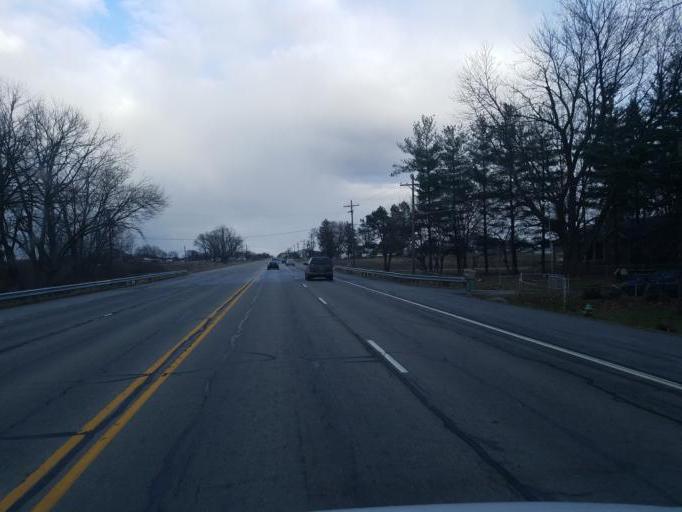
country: US
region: Indiana
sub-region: Marion County
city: Cumberland
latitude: 39.7781
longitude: -85.9249
